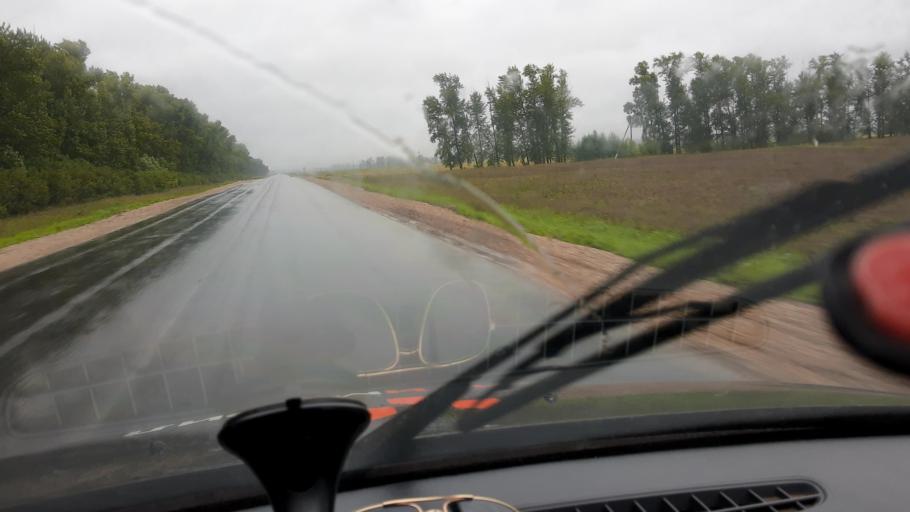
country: RU
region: Bashkortostan
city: Karmaskaly
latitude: 53.9608
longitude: 56.4000
